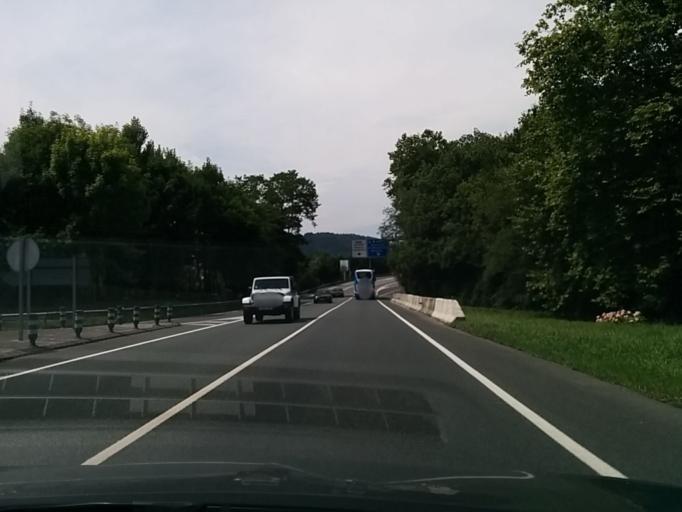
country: ES
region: Basque Country
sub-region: Provincia de Guipuzcoa
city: Irun
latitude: 43.3314
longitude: -1.8247
